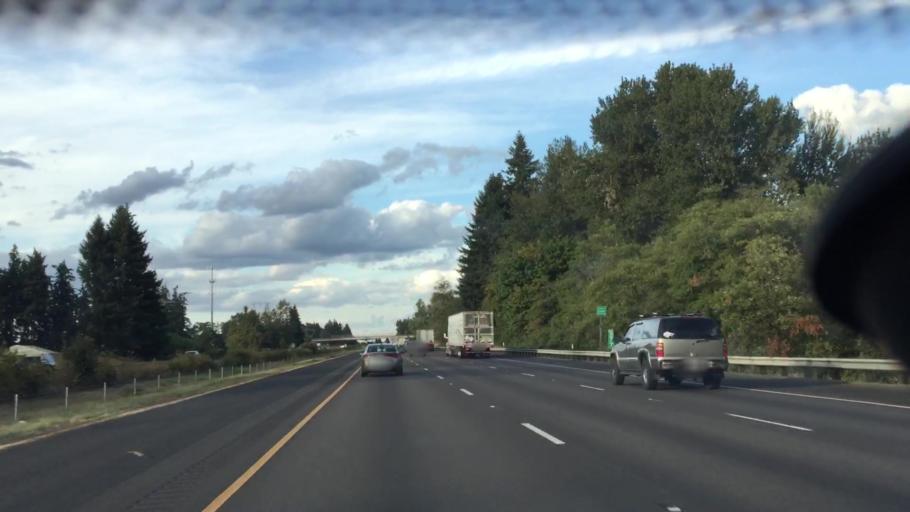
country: US
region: Oregon
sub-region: Marion County
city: Hubbard
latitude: 45.2124
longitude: -122.8238
